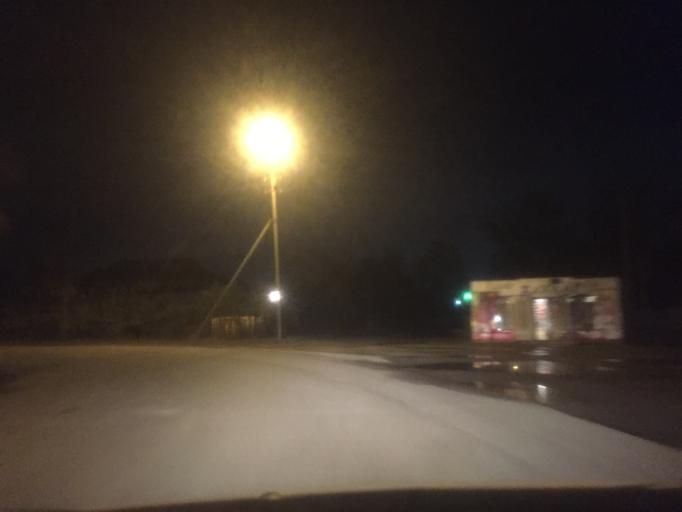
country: KZ
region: Astana Qalasy
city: Astana
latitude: 51.2113
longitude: 71.3848
